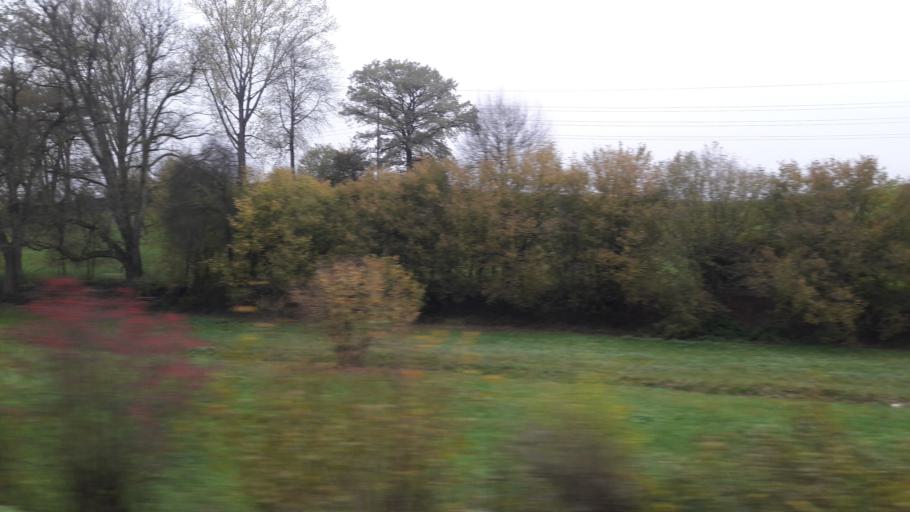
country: CH
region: Bern
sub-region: Oberaargau
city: Oberbipp
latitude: 47.2477
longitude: 7.6756
